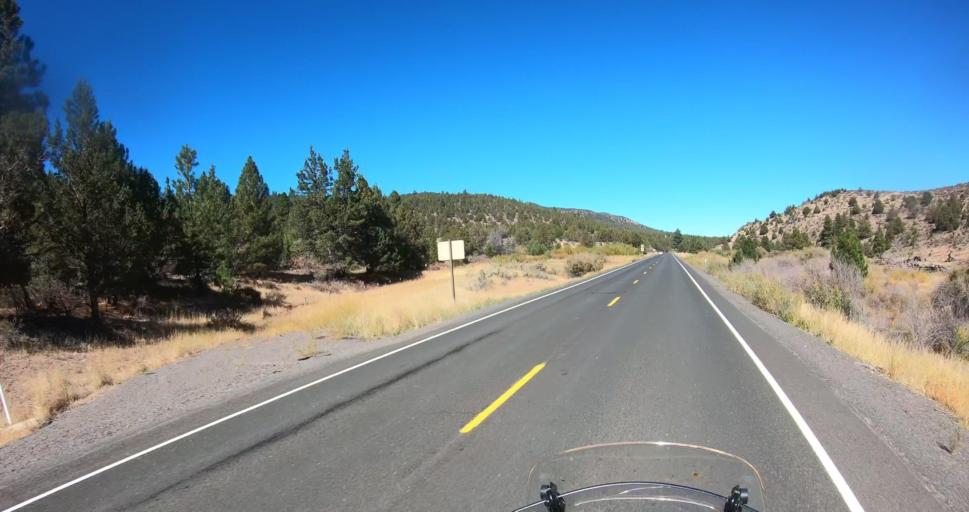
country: US
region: Oregon
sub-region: Lake County
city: Lakeview
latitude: 42.4165
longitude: -120.2899
